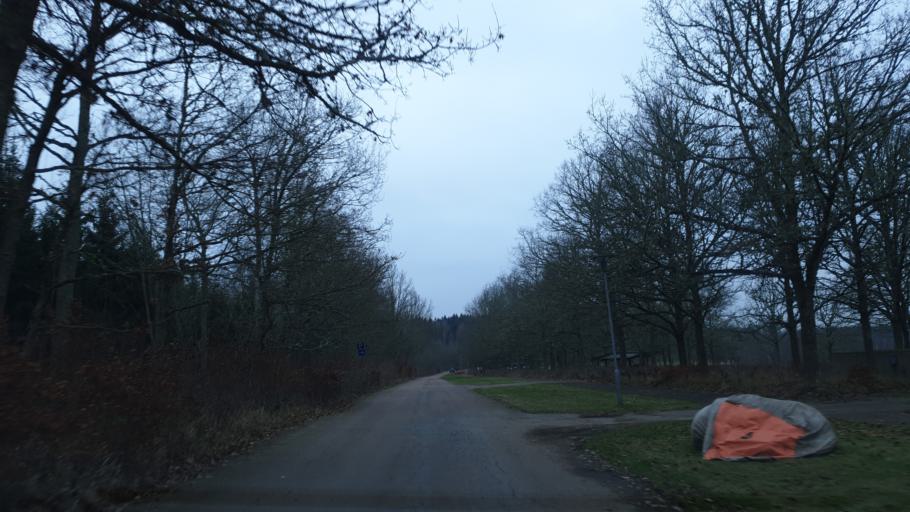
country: SE
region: Blekinge
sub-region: Karlskrona Kommun
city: Rodeby
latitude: 56.2139
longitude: 15.6838
